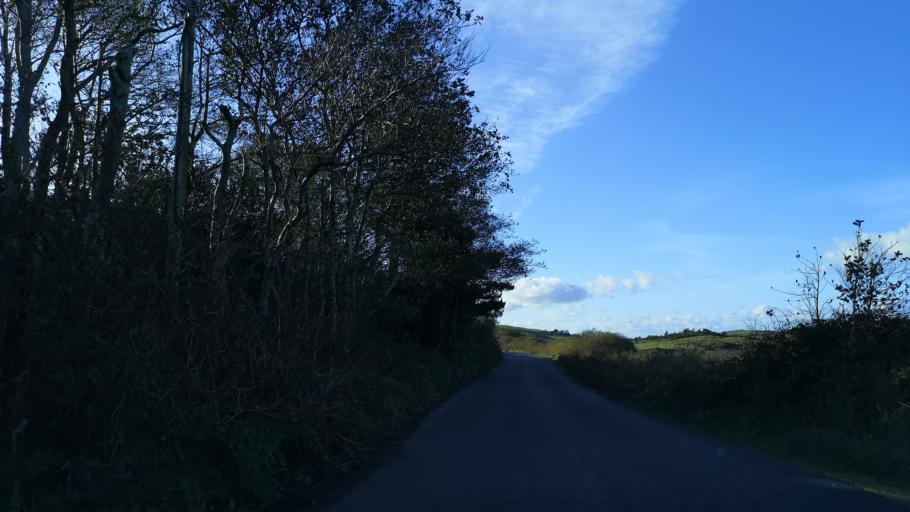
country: IE
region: Connaught
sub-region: County Galway
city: Clifden
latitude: 53.5059
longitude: -10.0749
